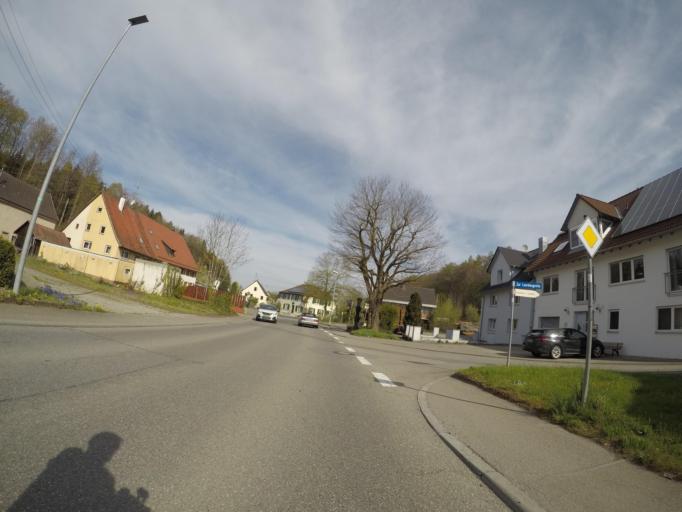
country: DE
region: Baden-Wuerttemberg
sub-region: Tuebingen Region
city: Allmannsweiler
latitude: 48.0072
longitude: 9.5632
